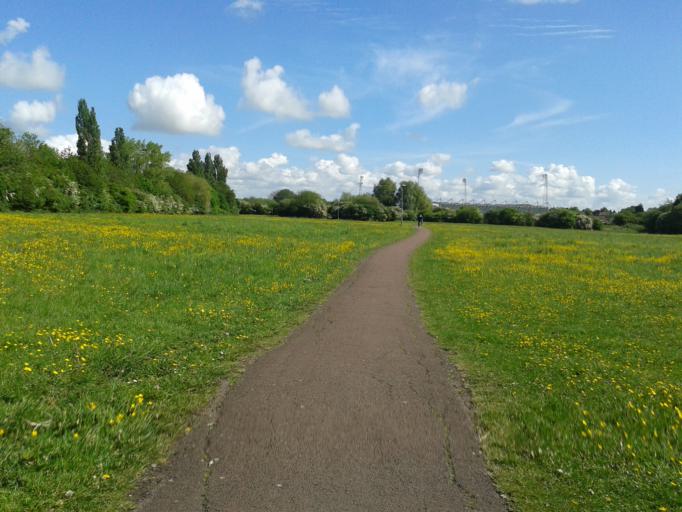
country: GB
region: England
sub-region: Cambridgeshire
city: Cambridge
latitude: 52.2085
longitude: 0.1502
